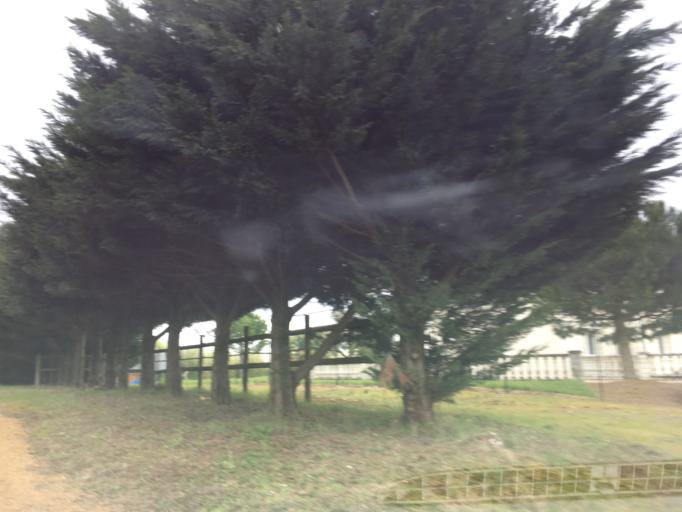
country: FR
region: Centre
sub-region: Departement d'Indre-et-Loire
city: Chanceaux-sur-Choisille
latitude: 47.4713
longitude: 0.6835
